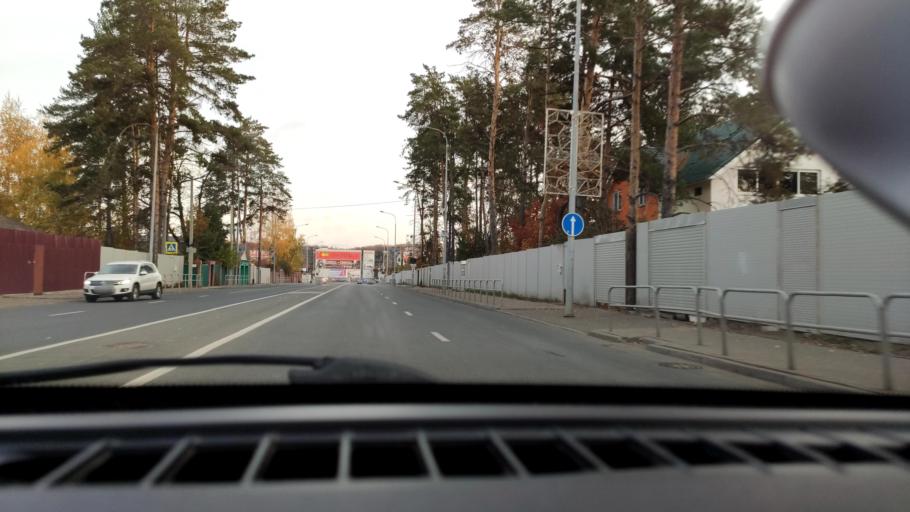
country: RU
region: Samara
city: Samara
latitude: 53.2660
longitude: 50.2420
